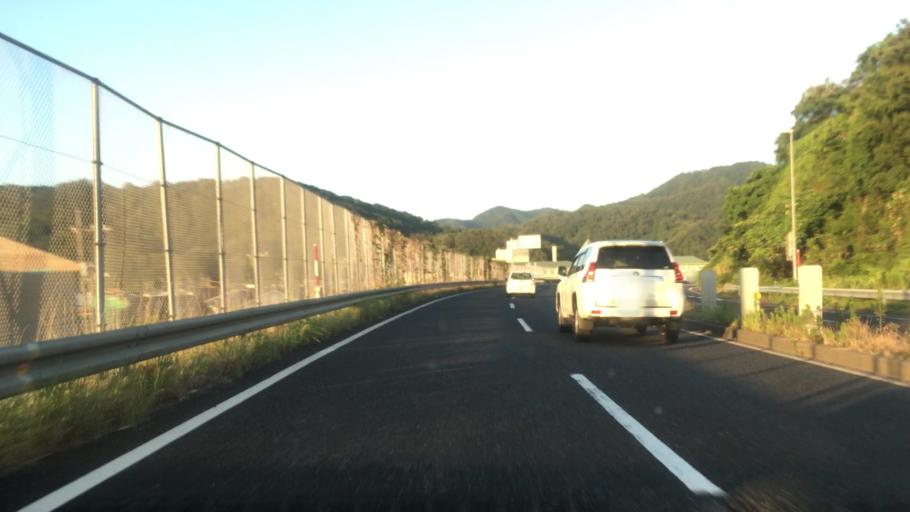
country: JP
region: Tottori
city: Tottori
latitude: 35.5239
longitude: 134.2228
